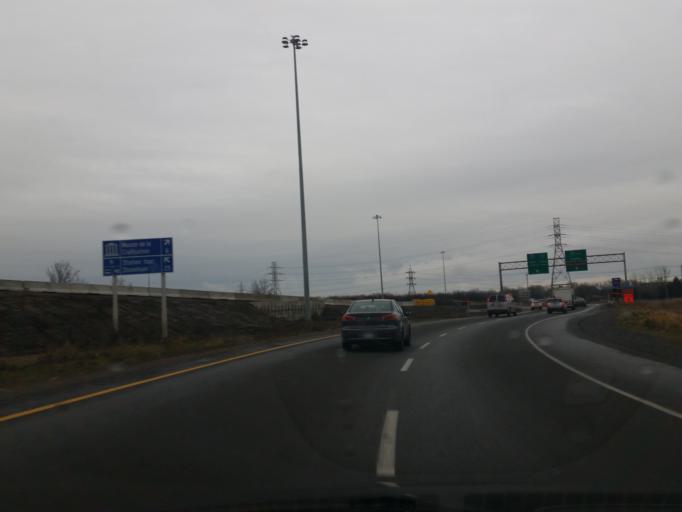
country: CA
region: Quebec
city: Quebec
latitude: 46.8353
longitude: -71.2669
